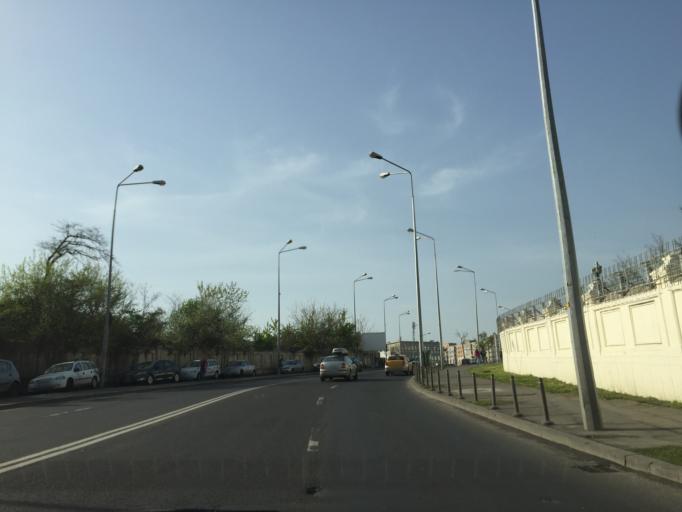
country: RO
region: Bucuresti
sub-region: Municipiul Bucuresti
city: Bucuresti
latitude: 44.4279
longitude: 26.0793
